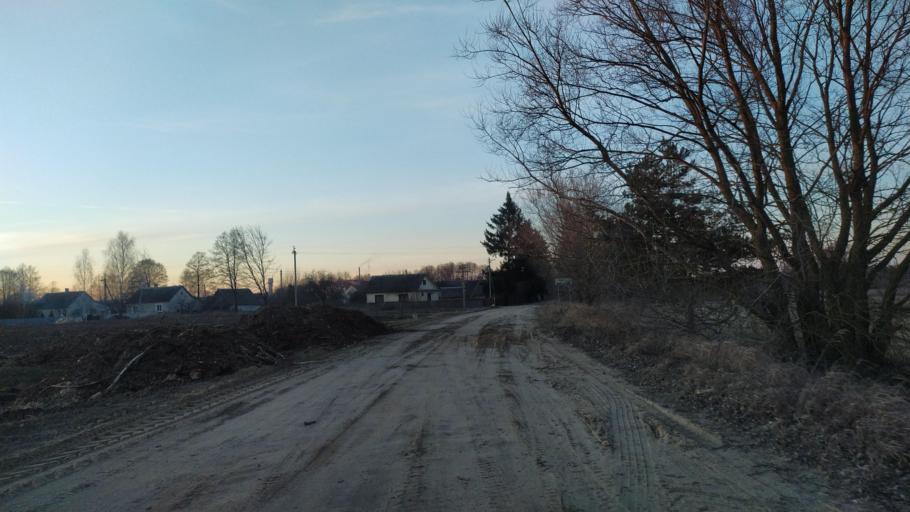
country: BY
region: Brest
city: Pruzhany
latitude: 52.5517
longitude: 24.2306
